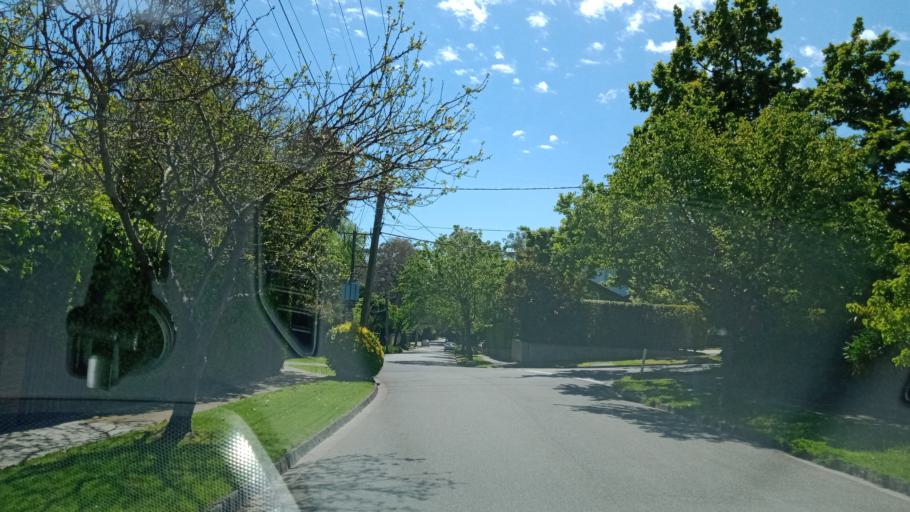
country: AU
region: Victoria
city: Toorak
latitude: -37.8408
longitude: 145.0273
